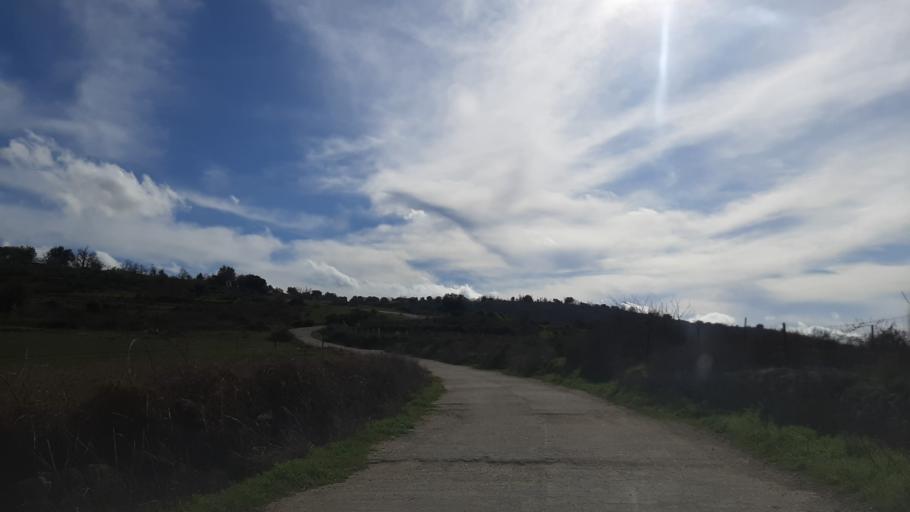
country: ES
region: Castille and Leon
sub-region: Provincia de Salamanca
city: Villarino de los Aires
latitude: 41.2564
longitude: -6.5268
